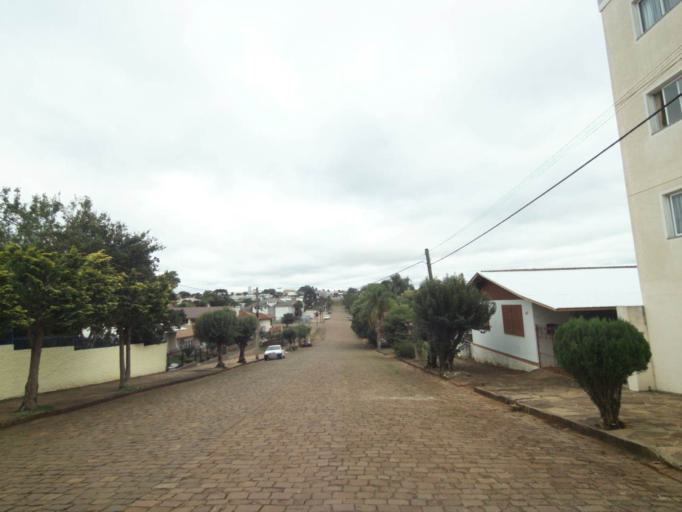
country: BR
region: Rio Grande do Sul
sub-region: Lagoa Vermelha
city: Lagoa Vermelha
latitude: -28.2092
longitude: -51.5187
